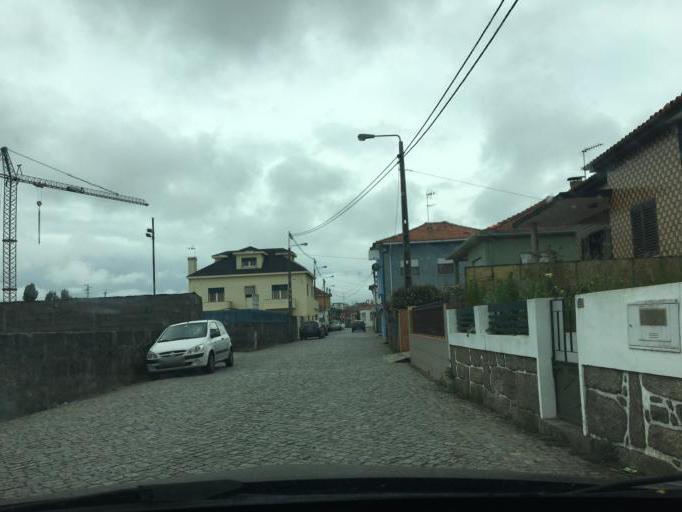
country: PT
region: Porto
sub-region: Matosinhos
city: Santa Cruz do Bispo
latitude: 41.2309
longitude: -8.6606
